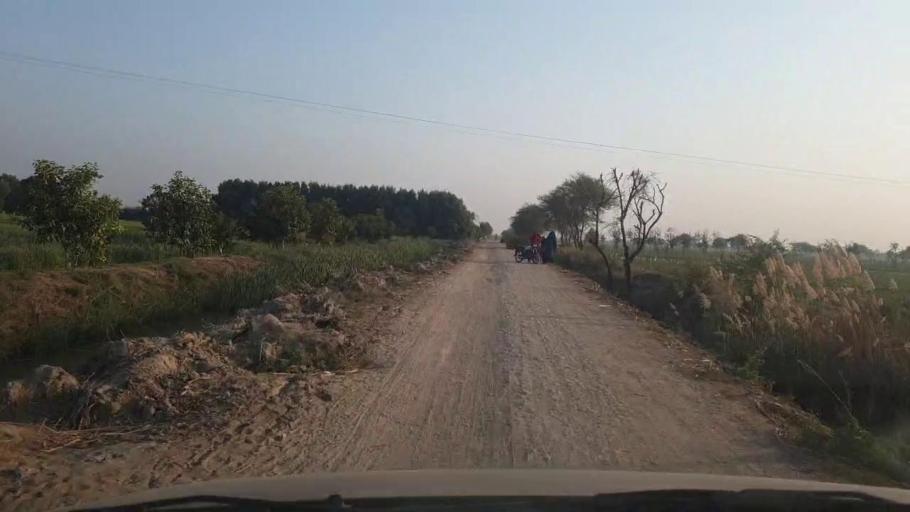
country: PK
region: Sindh
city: Mirwah Gorchani
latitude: 25.3573
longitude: 69.1527
